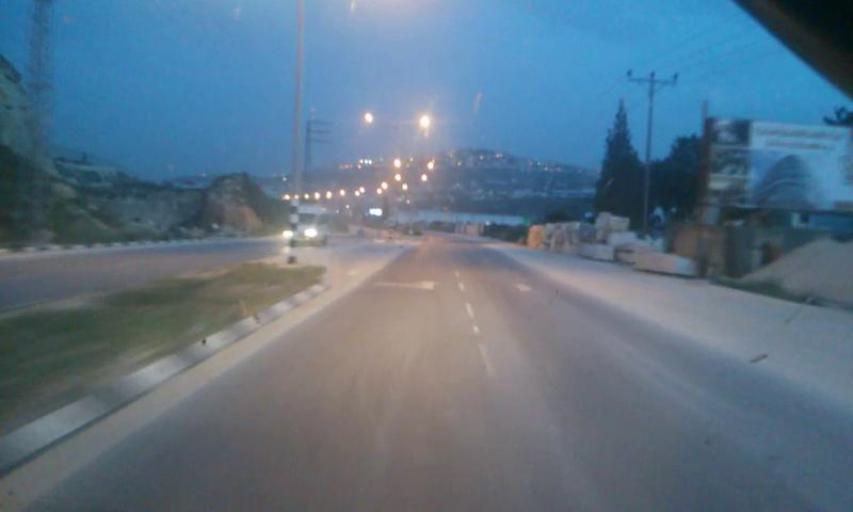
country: PS
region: West Bank
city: Dayr Sharaf
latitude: 32.2446
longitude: 35.1952
